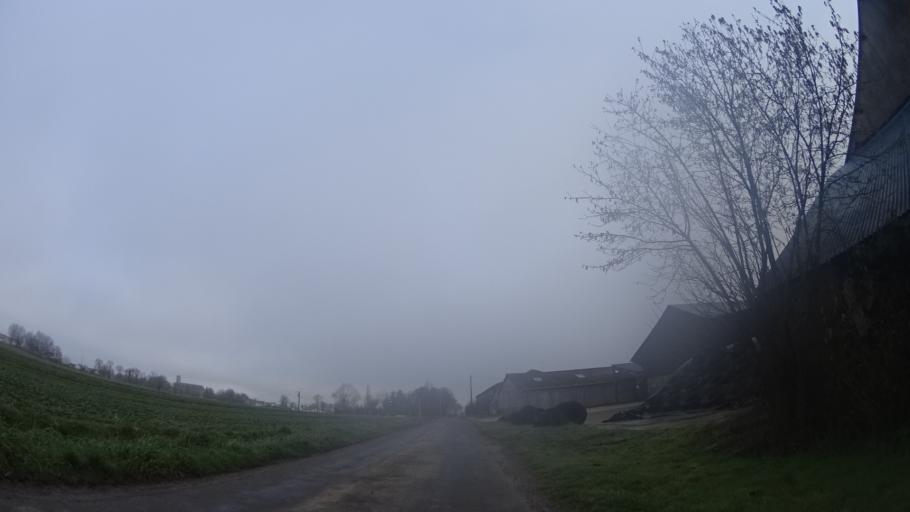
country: FR
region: Brittany
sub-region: Departement d'Ille-et-Vilaine
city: Saint-Domineuc
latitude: 48.3332
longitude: -1.9285
